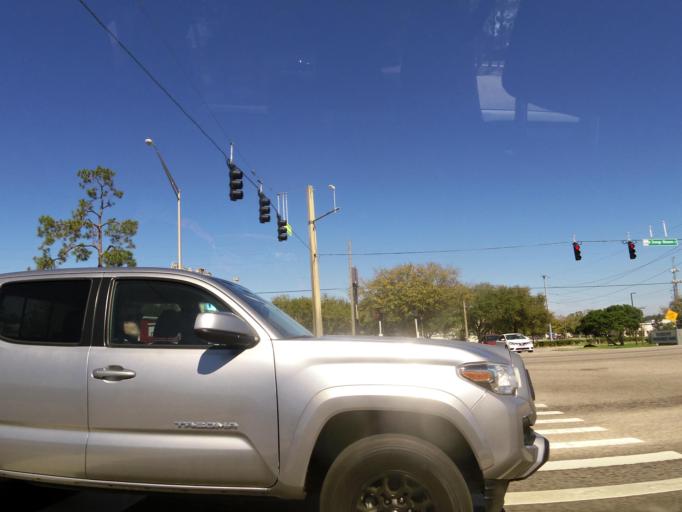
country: US
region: Florida
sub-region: Orange County
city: Lockhart
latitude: 28.6105
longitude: -81.4286
